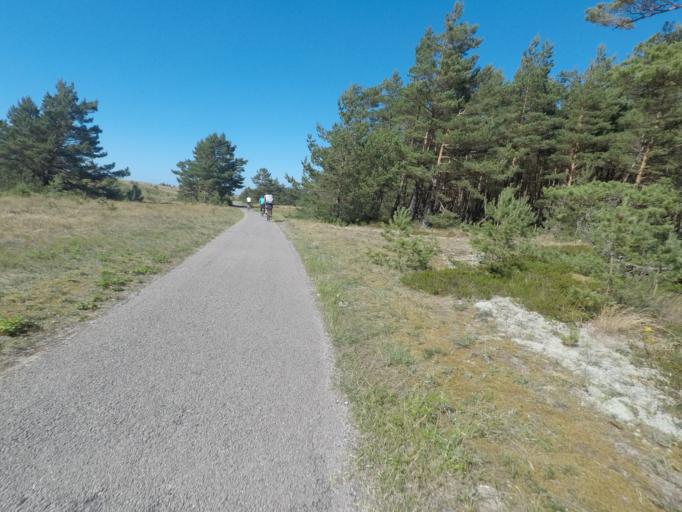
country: LT
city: Neringa
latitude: 55.5030
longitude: 21.0905
